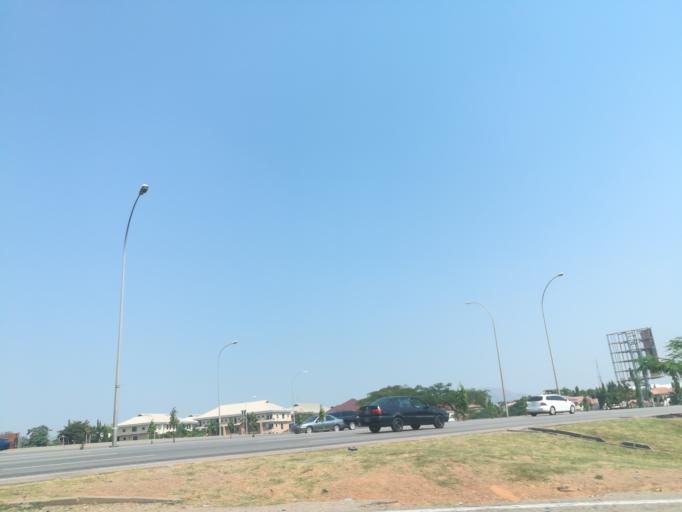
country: NG
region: Abuja Federal Capital Territory
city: Abuja
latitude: 9.0772
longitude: 7.4572
